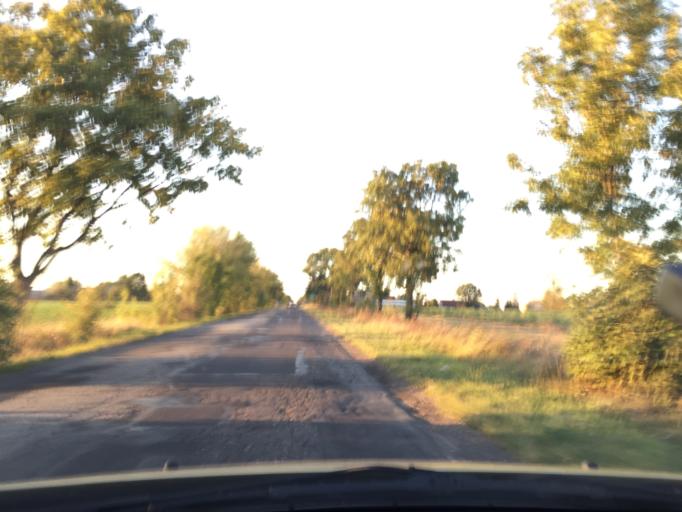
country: PL
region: Greater Poland Voivodeship
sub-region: Powiat pleszewski
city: Dobrzyca
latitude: 51.8386
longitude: 17.6204
